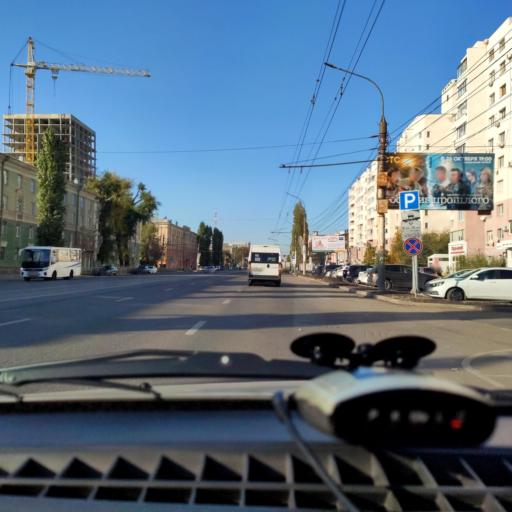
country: RU
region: Voronezj
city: Voronezh
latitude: 51.6475
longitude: 39.1966
